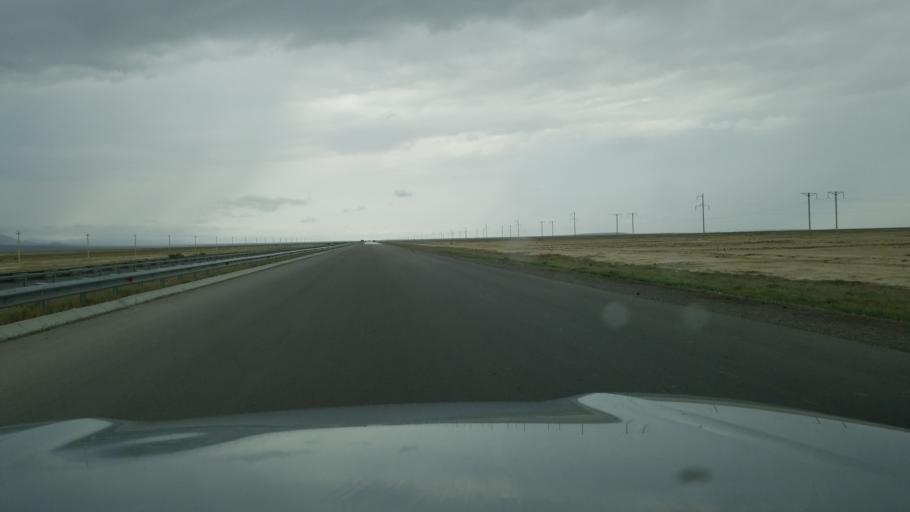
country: TM
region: Balkan
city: Serdar
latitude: 39.0485
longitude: 56.1341
